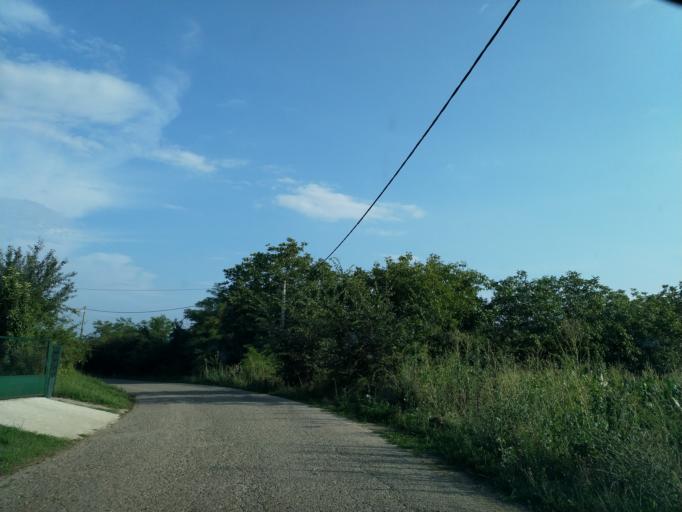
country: RS
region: Central Serbia
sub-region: Pomoravski Okrug
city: Jagodina
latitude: 44.0034
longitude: 21.1839
